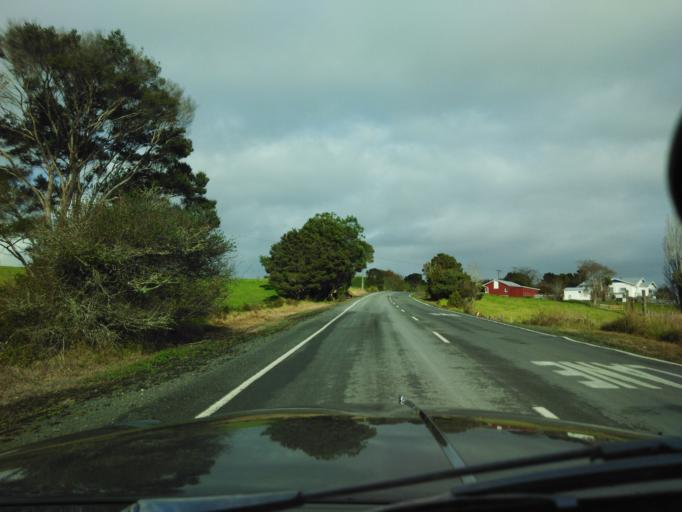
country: NZ
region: Auckland
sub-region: Auckland
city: Wellsford
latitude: -36.2900
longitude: 174.4284
